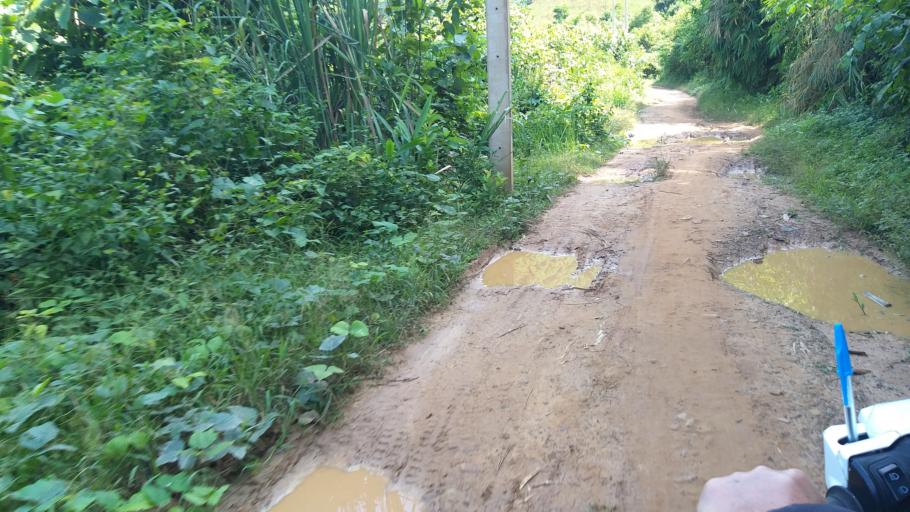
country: LA
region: Phongsali
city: Khoa
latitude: 21.3299
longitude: 102.5663
